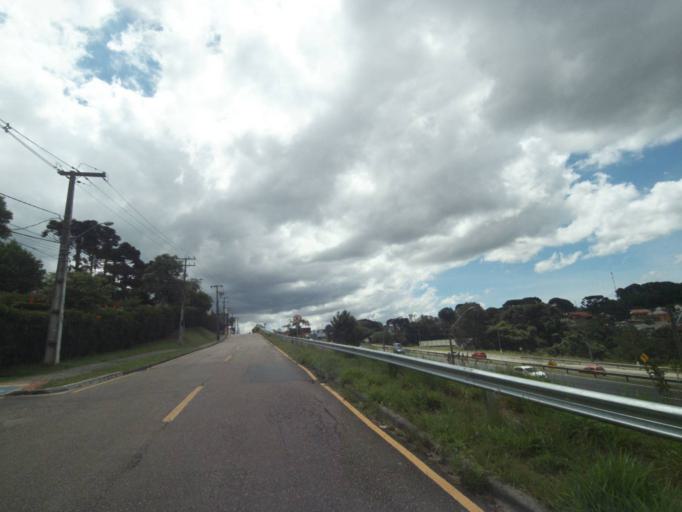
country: BR
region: Parana
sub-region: Curitiba
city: Curitiba
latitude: -25.4313
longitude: -49.3257
